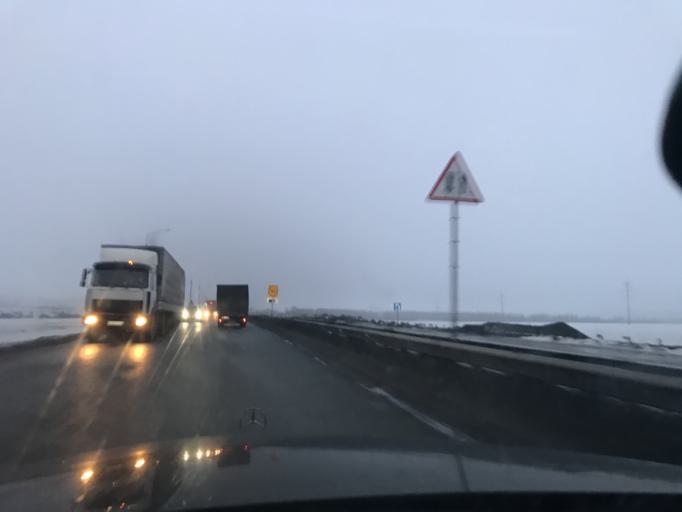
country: RU
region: Vladimir
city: Novovyazniki
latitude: 56.2176
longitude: 42.2217
